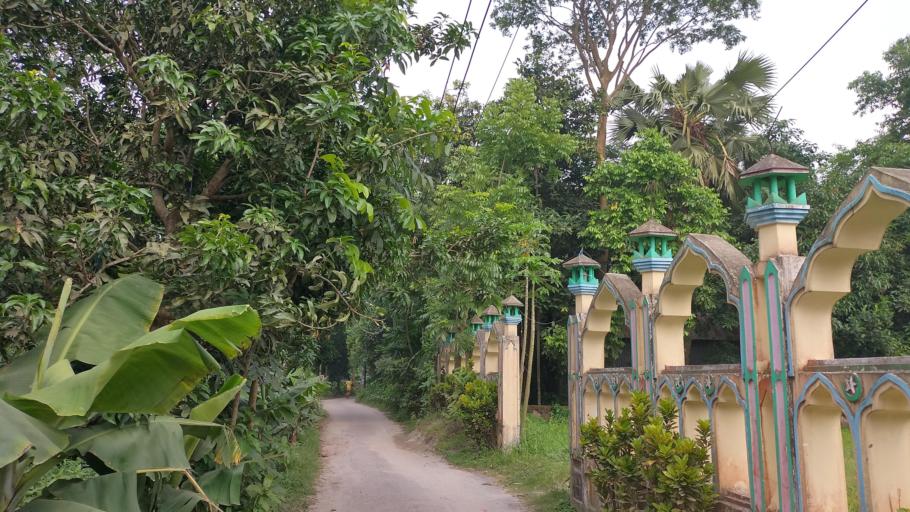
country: BD
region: Dhaka
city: Azimpur
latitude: 23.6939
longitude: 90.2989
